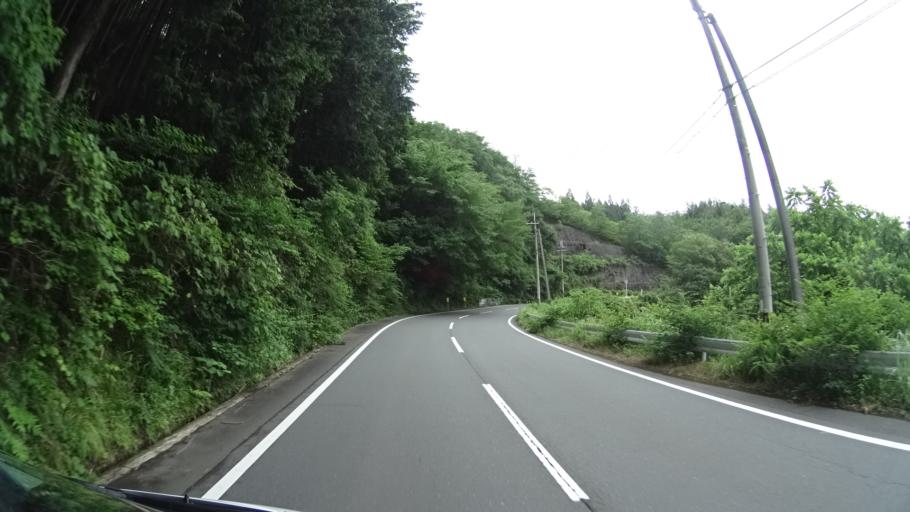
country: JP
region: Kyoto
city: Kameoka
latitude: 35.0808
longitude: 135.4111
